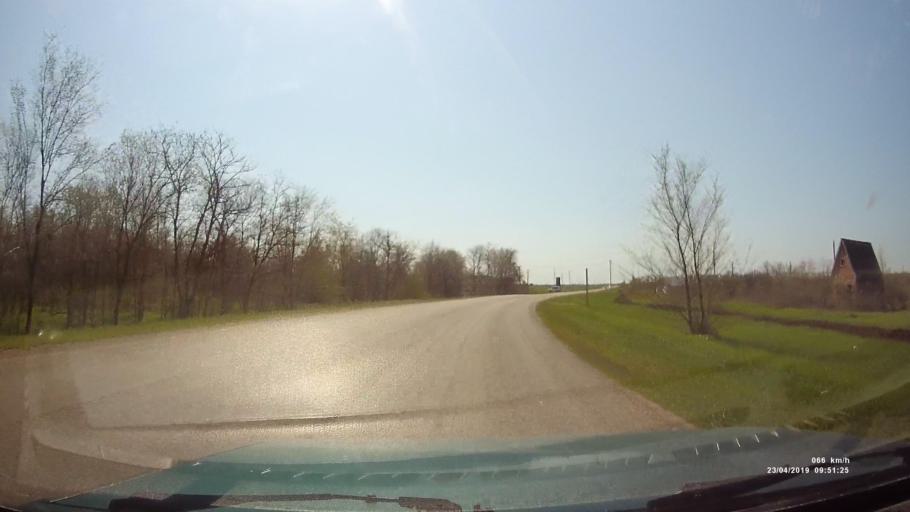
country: RU
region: Rostov
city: Orlovskiy
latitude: 46.8556
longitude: 42.0408
